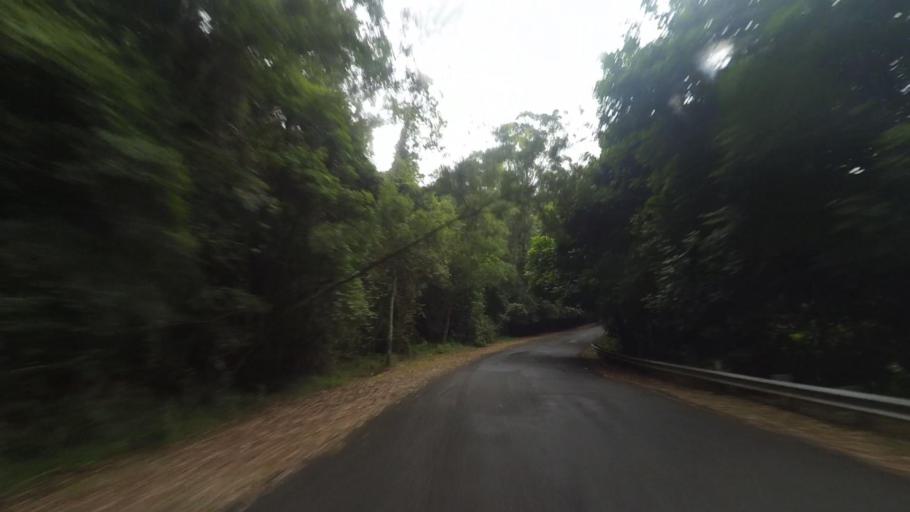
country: AU
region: New South Wales
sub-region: Wollongong
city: Cordeaux Heights
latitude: -34.4149
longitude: 150.8174
